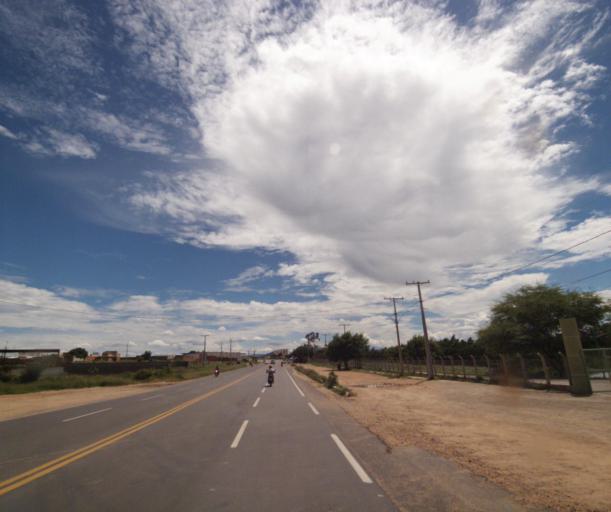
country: BR
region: Bahia
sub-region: Guanambi
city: Guanambi
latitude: -14.2254
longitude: -42.7635
